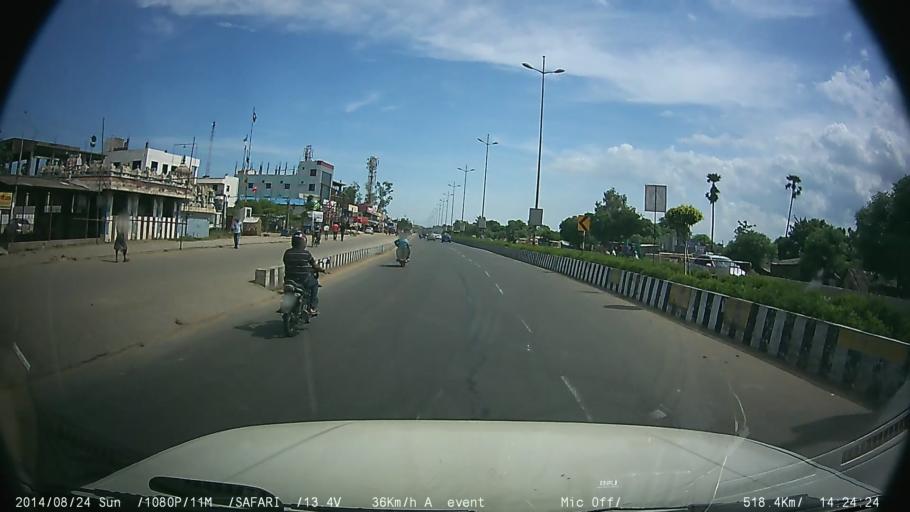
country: IN
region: Tamil Nadu
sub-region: Kancheepuram
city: Injambakkam
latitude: 12.8855
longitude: 80.2268
